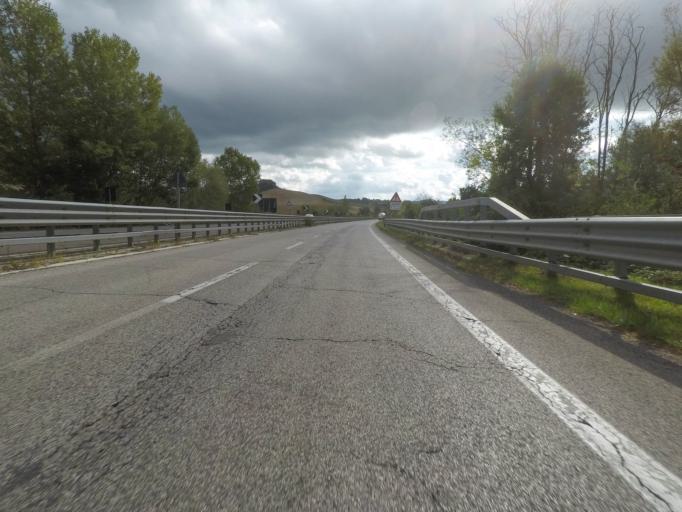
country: IT
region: Tuscany
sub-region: Provincia di Siena
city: Rapolano Terme
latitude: 43.3218
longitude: 11.5681
